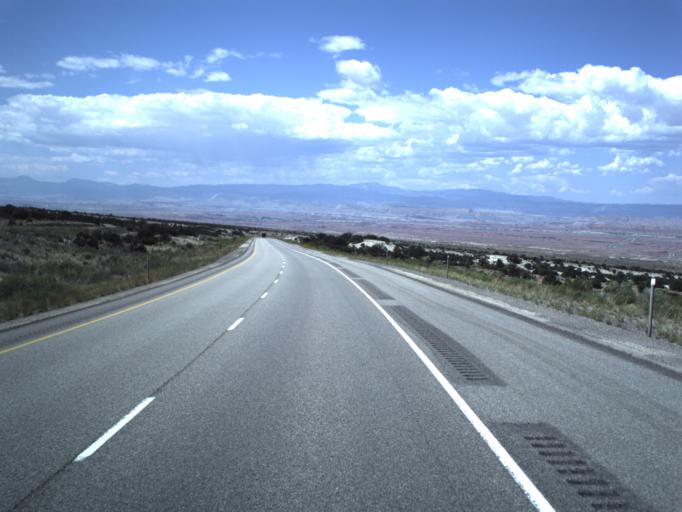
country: US
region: Utah
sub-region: Emery County
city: Ferron
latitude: 38.8467
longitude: -110.9425
